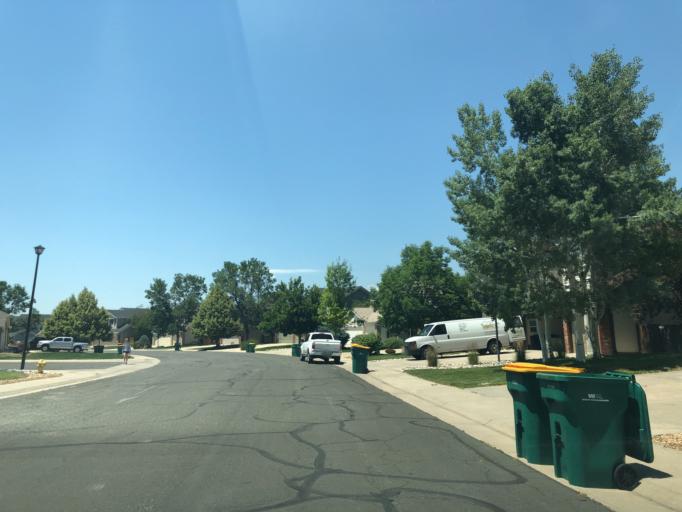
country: US
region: Colorado
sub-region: Arapahoe County
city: Dove Valley
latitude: 39.6314
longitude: -104.7662
